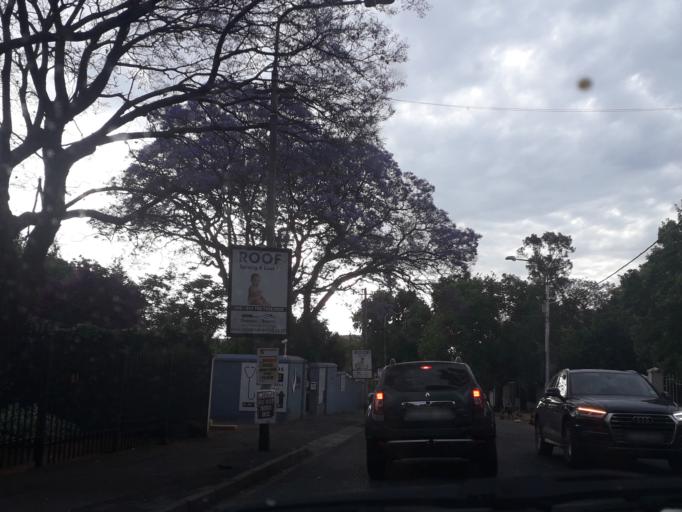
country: ZA
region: Gauteng
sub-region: City of Johannesburg Metropolitan Municipality
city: Johannesburg
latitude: -26.1447
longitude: 28.0246
